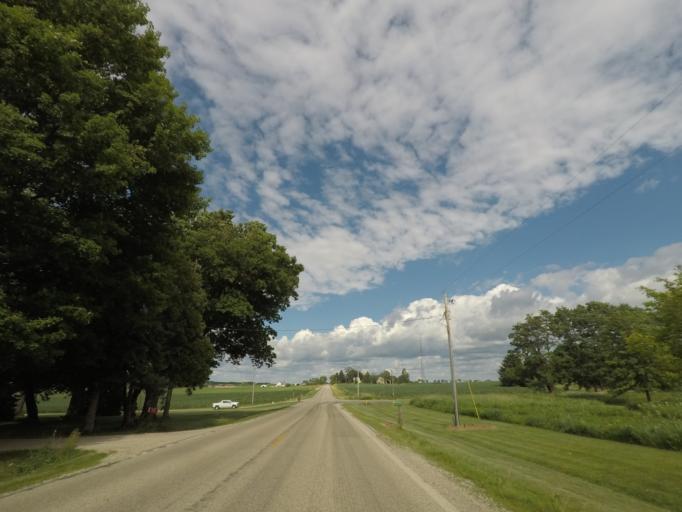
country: US
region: Wisconsin
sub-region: Rock County
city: Janesville
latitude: 42.7012
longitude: -89.1027
